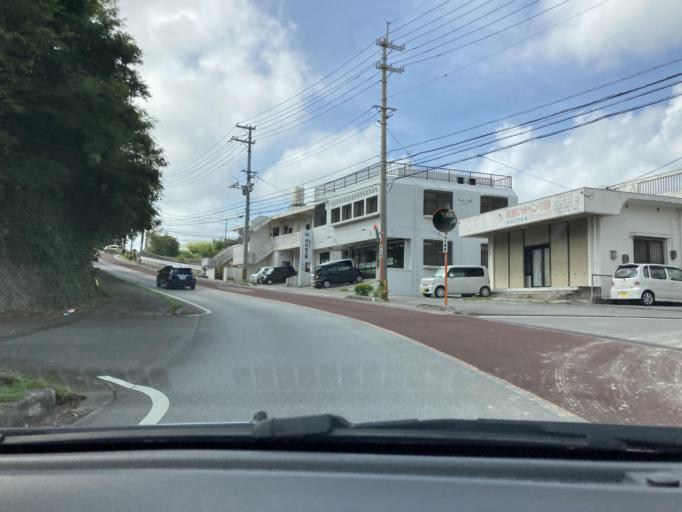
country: JP
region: Okinawa
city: Okinawa
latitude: 26.3193
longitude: 127.8049
